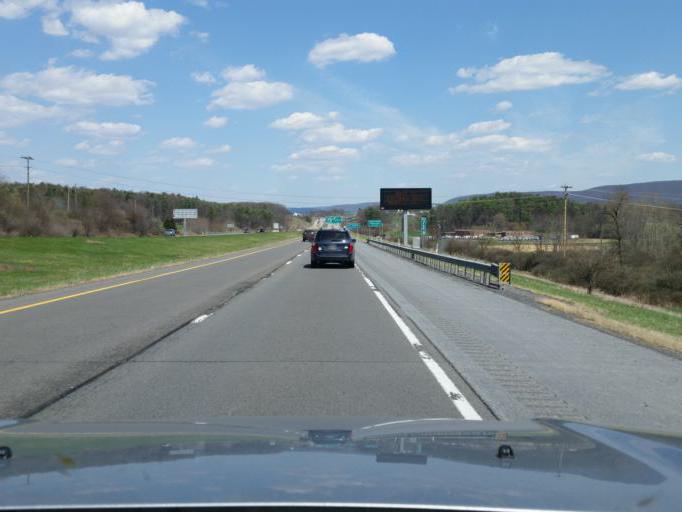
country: US
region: Pennsylvania
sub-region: Centre County
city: State College
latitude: 40.8212
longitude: -77.8744
